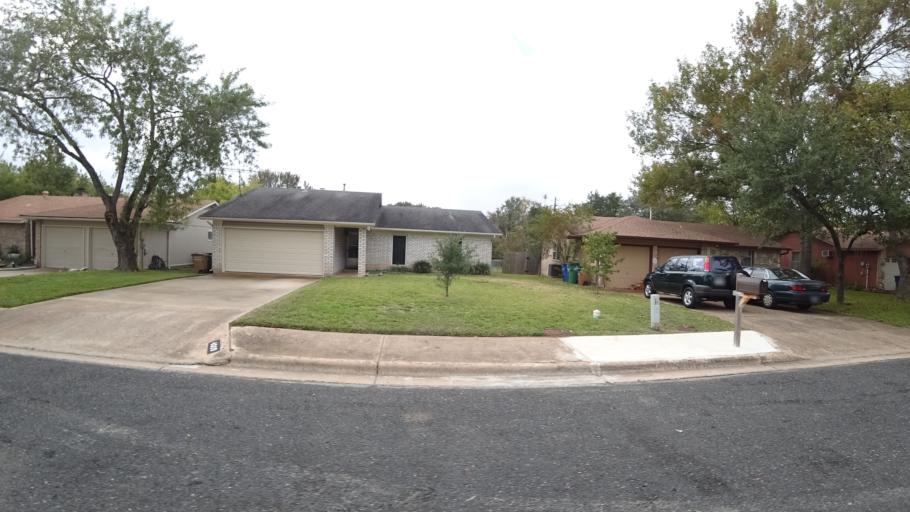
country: US
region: Texas
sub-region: Travis County
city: Shady Hollow
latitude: 30.2110
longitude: -97.8410
